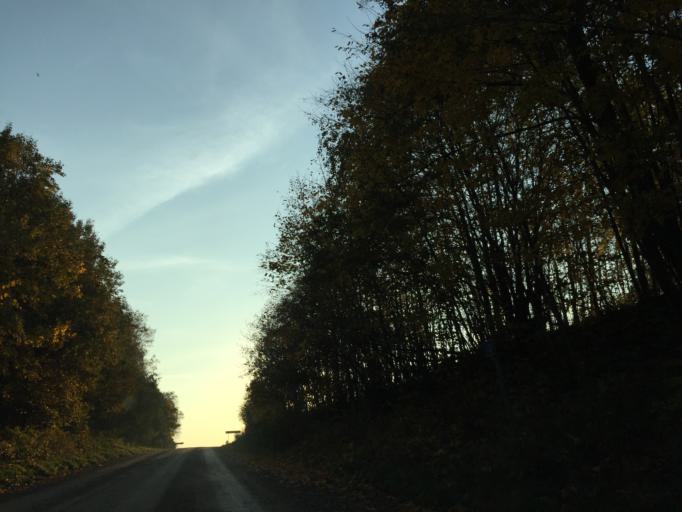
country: LV
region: Vainode
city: Vainode
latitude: 56.5001
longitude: 21.8053
